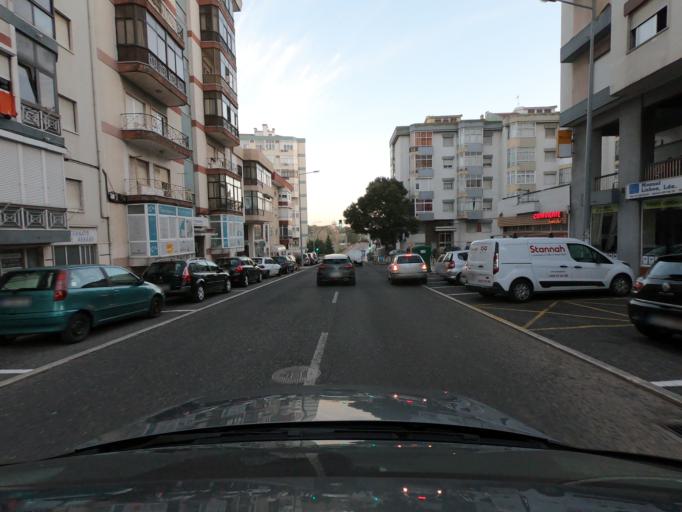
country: PT
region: Lisbon
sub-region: Sintra
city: Queluz
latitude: 38.7572
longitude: -9.2676
